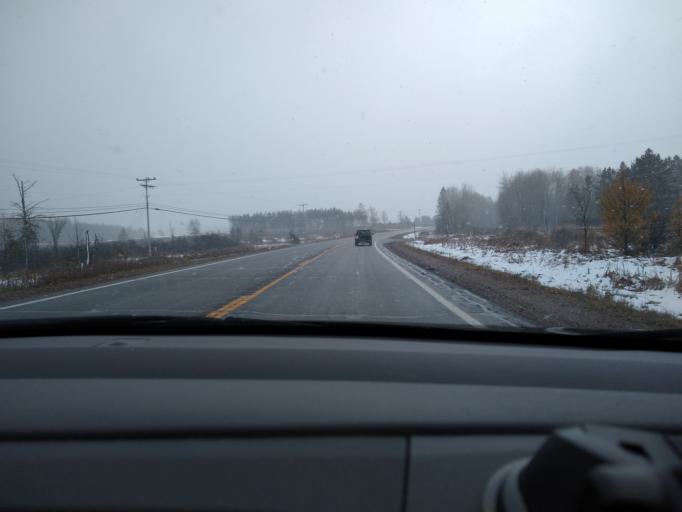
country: US
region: Wisconsin
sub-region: Florence County
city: Florence
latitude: 46.0808
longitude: -88.0747
